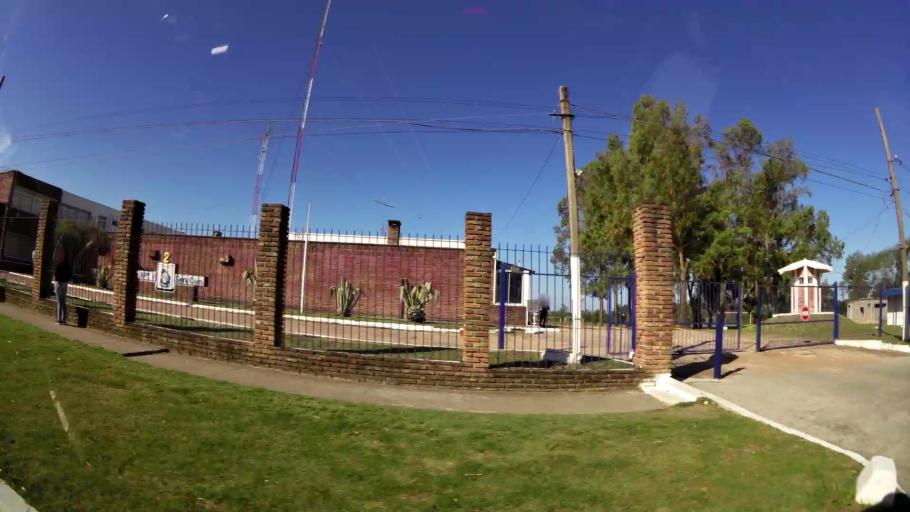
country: UY
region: Canelones
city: La Paz
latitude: -34.8265
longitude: -56.1966
